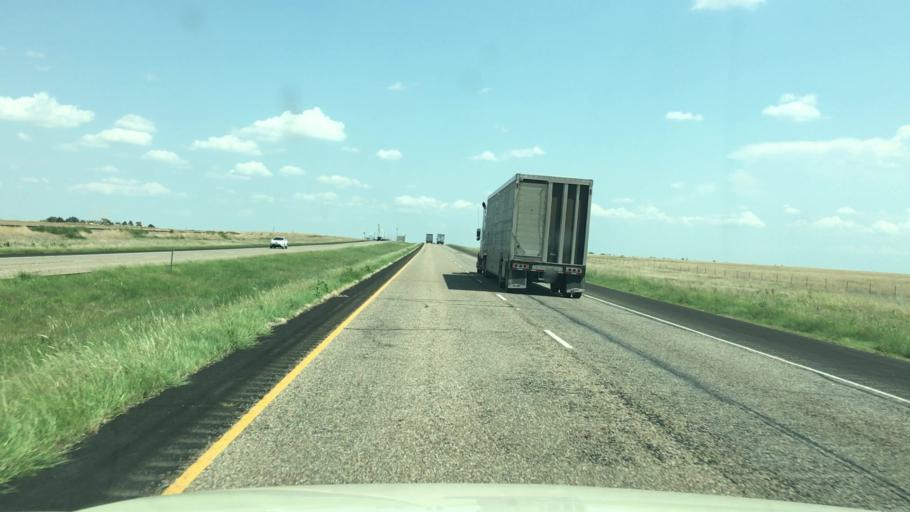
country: US
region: Texas
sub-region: Armstrong County
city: Claude
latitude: 35.1251
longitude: -101.3964
